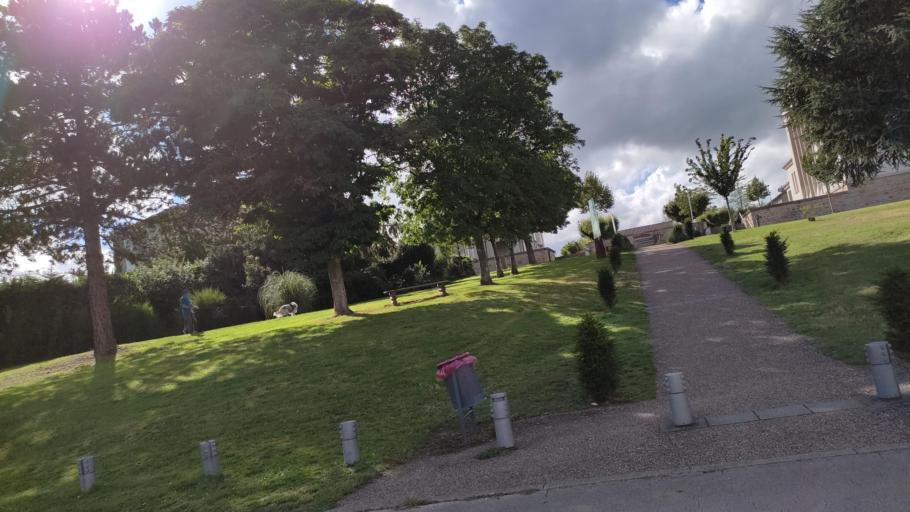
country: FR
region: Limousin
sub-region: Departement de la Haute-Vienne
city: Oradour-sur-Glane
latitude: 45.9296
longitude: 1.0346
